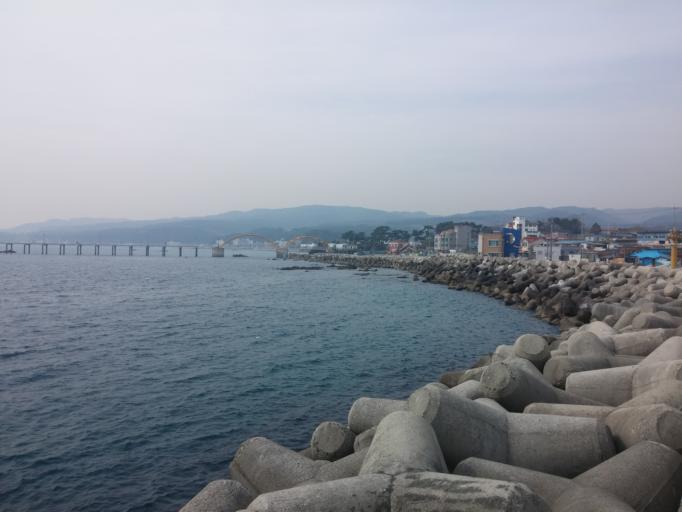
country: KR
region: Ulsan
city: Ulsan
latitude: 35.5832
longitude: 129.4584
